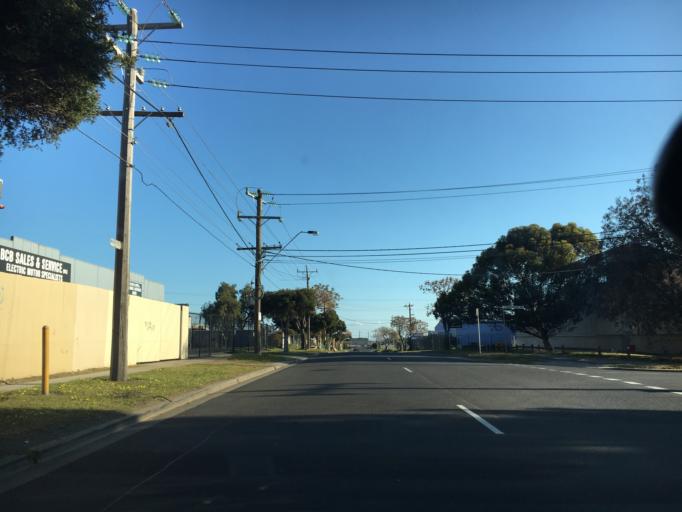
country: AU
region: Victoria
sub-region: Kingston
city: Clayton South
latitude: -37.9390
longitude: 145.1267
